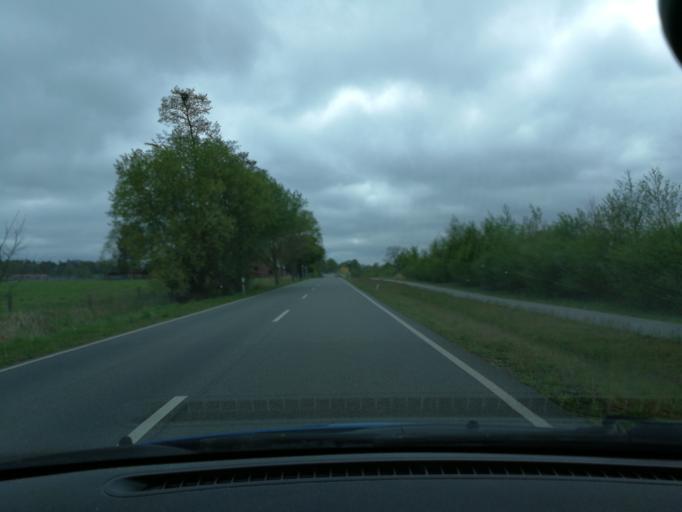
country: DE
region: Schleswig-Holstein
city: Hollenbek
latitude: 53.5042
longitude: 10.8371
